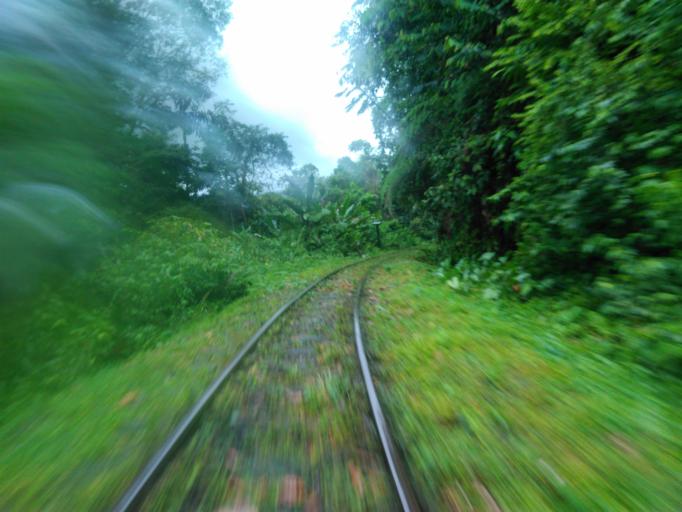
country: CO
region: Valle del Cauca
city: Buenaventura
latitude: 3.8486
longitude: -76.8839
